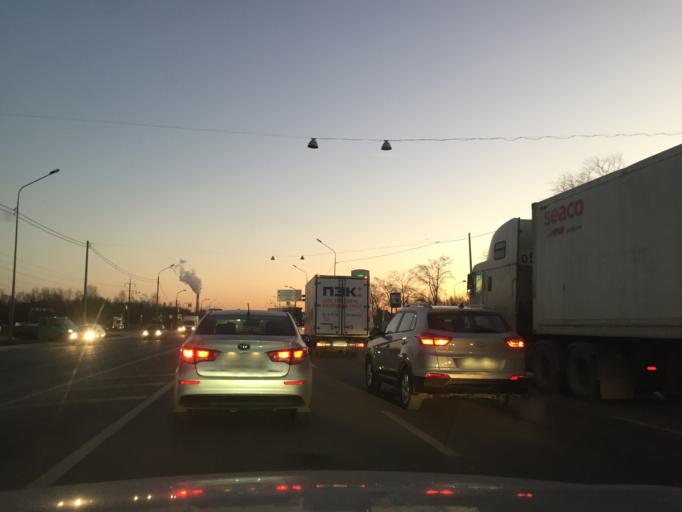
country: RU
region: St.-Petersburg
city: Obukhovo
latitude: 59.8532
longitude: 30.4254
